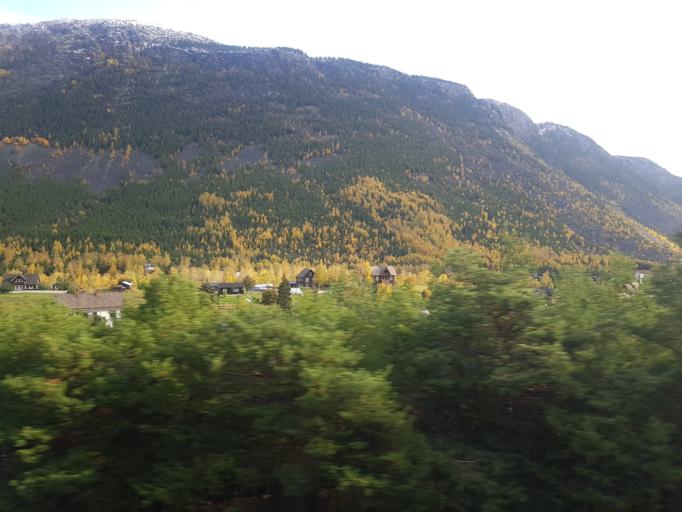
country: NO
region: Oppland
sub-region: Sel
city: Otta
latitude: 61.8489
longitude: 9.4159
